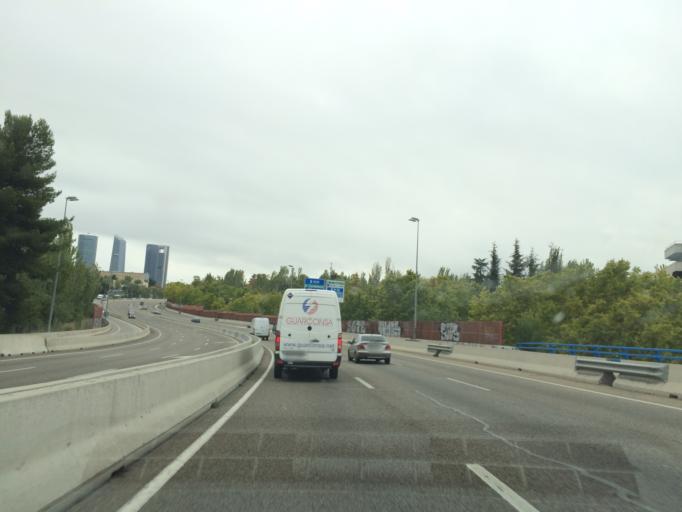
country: ES
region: Madrid
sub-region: Provincia de Madrid
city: Las Tablas
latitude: 40.4957
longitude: -3.7007
